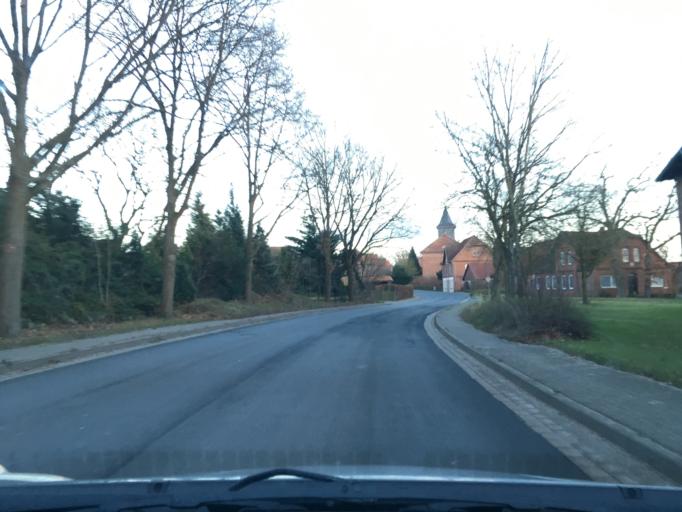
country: DE
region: Lower Saxony
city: Ratzlingen
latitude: 52.9760
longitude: 10.6699
